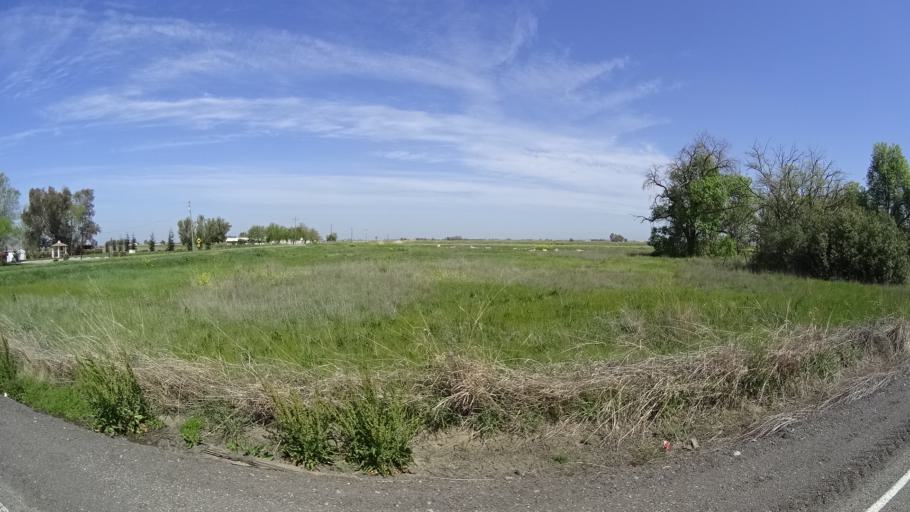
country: US
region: California
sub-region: Glenn County
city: Willows
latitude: 39.5825
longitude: -122.0457
